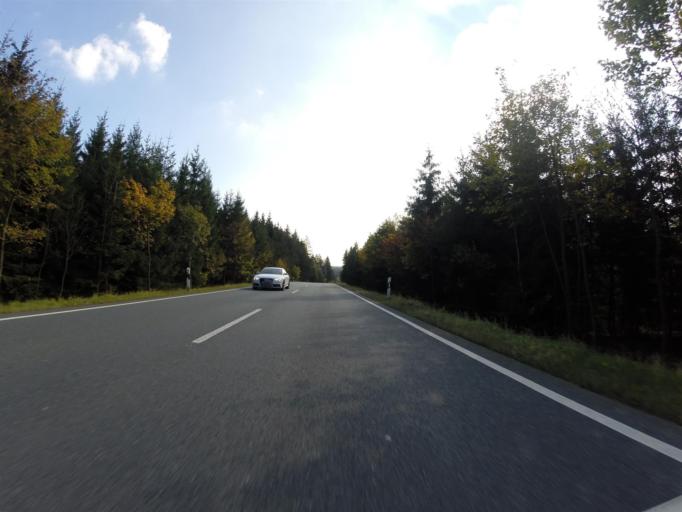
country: DE
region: Thuringia
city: Tanna
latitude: 50.4743
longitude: 11.8391
